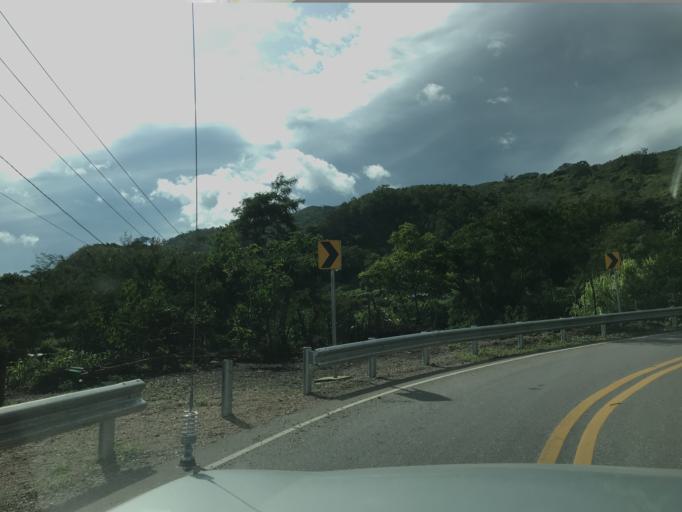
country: TL
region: Aileu
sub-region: Aileu Villa
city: Aileu
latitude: -8.8011
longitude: 125.5789
